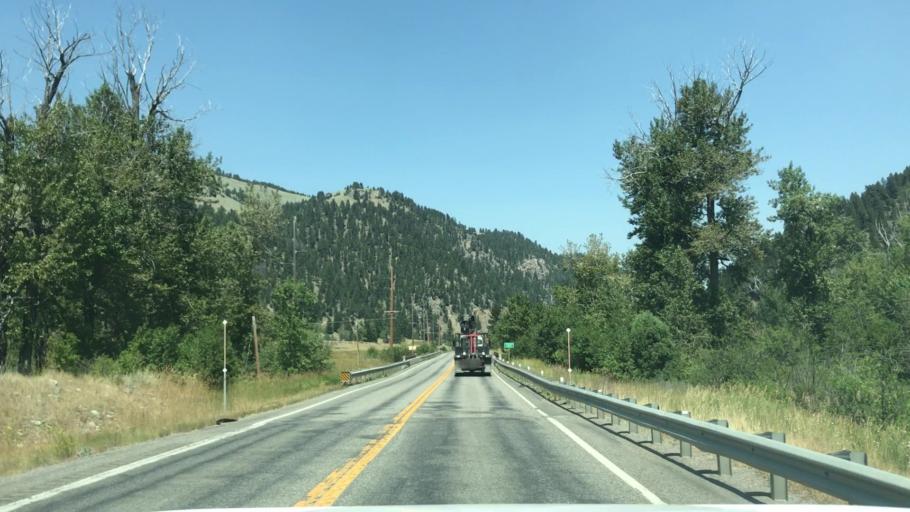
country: US
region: Montana
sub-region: Gallatin County
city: Four Corners
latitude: 45.4930
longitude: -111.2723
